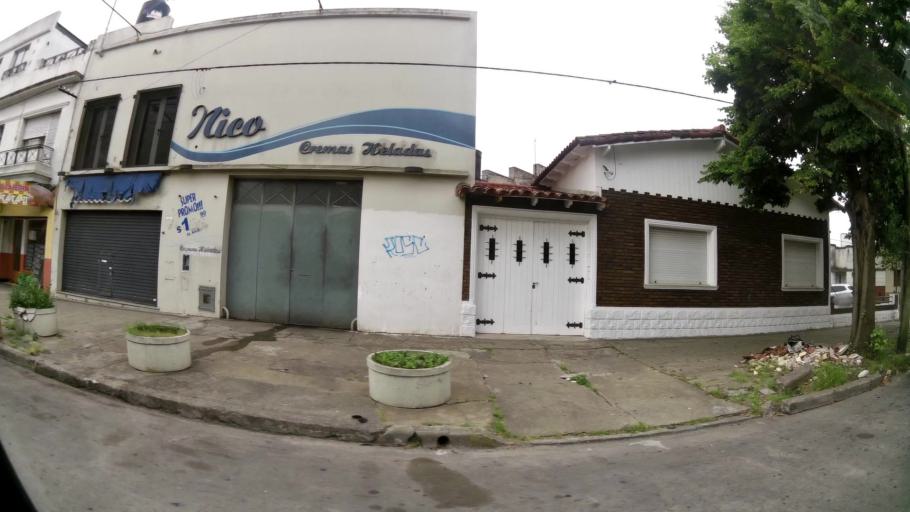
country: AR
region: Buenos Aires
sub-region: Partido de La Plata
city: La Plata
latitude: -34.9223
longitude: -57.9768
